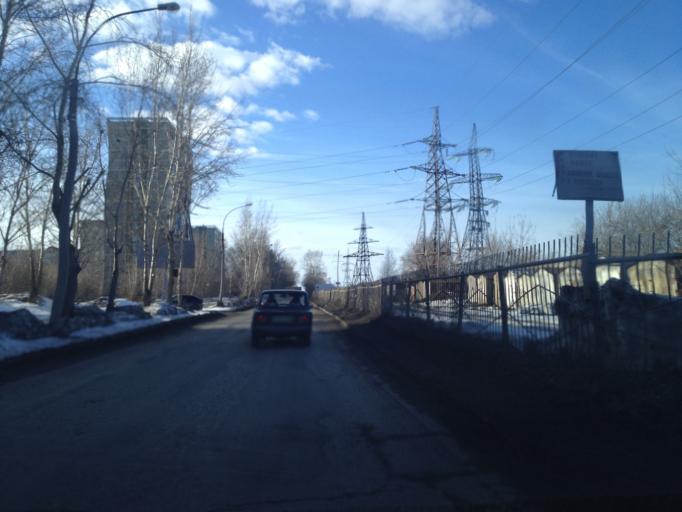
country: RU
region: Sverdlovsk
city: Yekaterinburg
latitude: 56.8716
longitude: 60.5607
